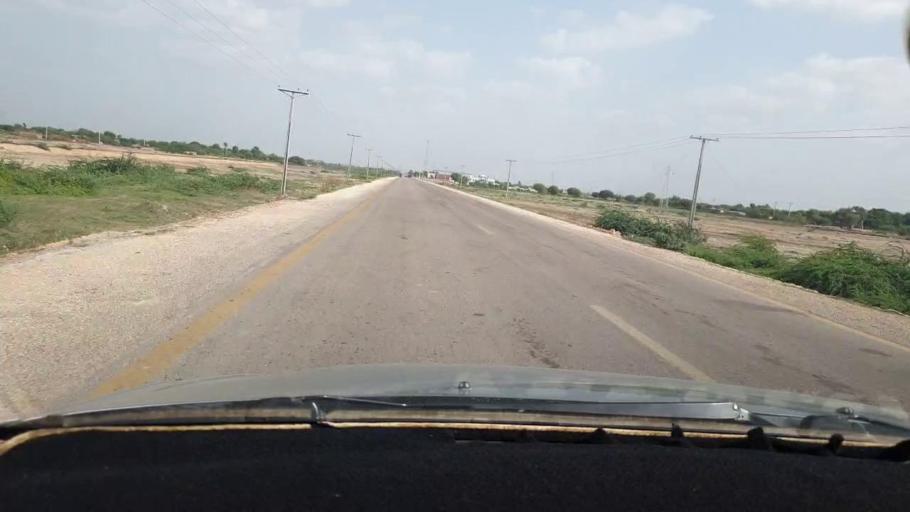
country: PK
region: Sindh
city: Naukot
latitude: 24.8701
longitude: 69.3766
